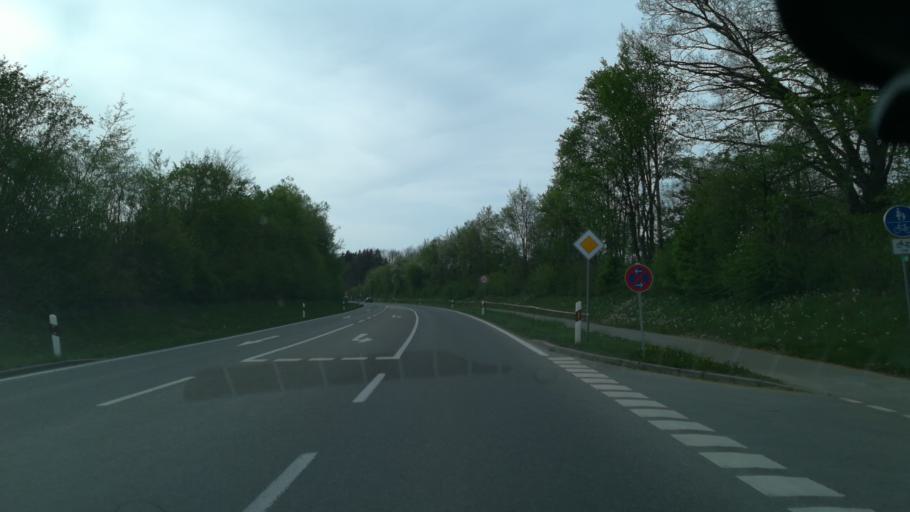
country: DE
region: Baden-Wuerttemberg
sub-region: Freiburg Region
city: Moos
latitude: 47.7554
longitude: 8.9136
